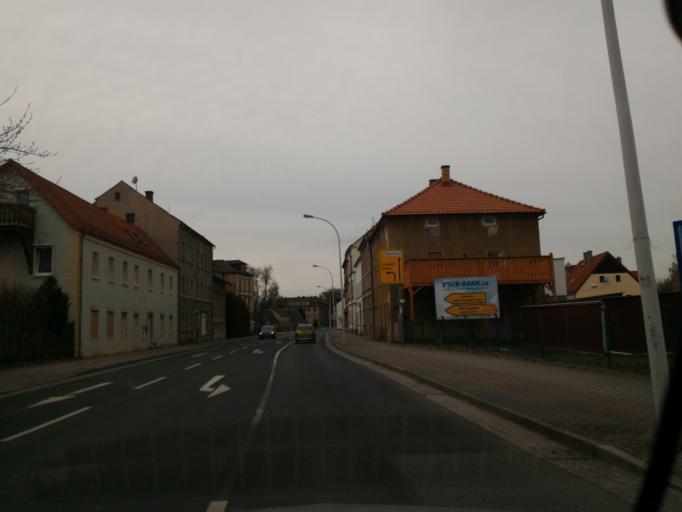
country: DE
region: Saxony
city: Zittau
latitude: 50.8857
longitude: 14.8160
